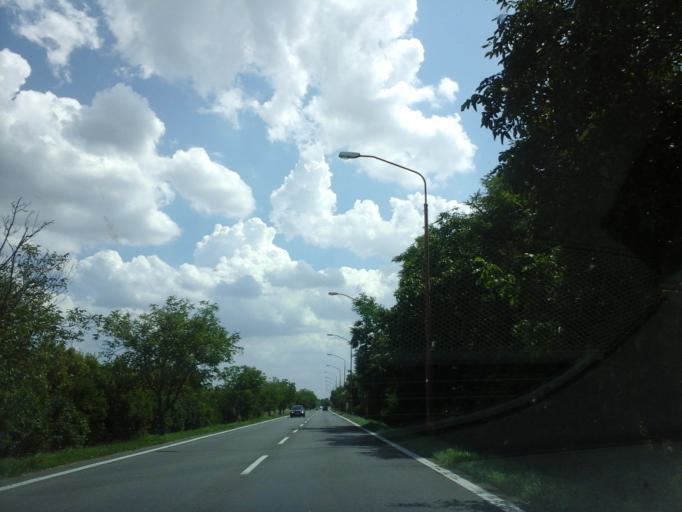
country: HU
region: Gyor-Moson-Sopron
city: Rajka
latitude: 48.0407
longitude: 17.1586
